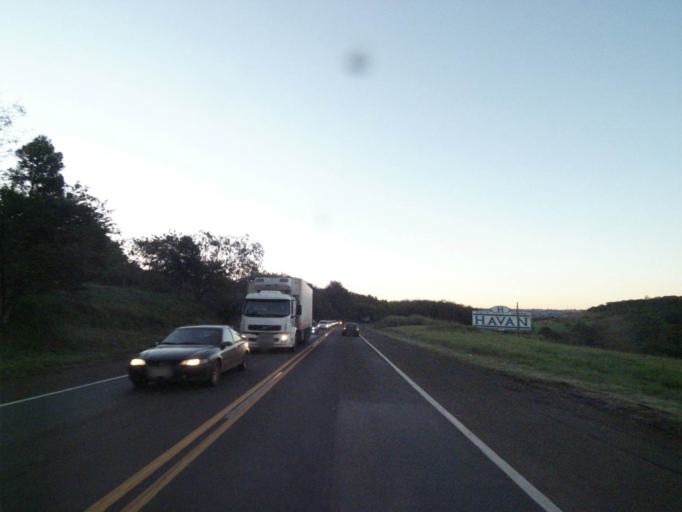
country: BR
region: Parana
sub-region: Londrina
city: Londrina
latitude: -23.4264
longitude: -51.1398
